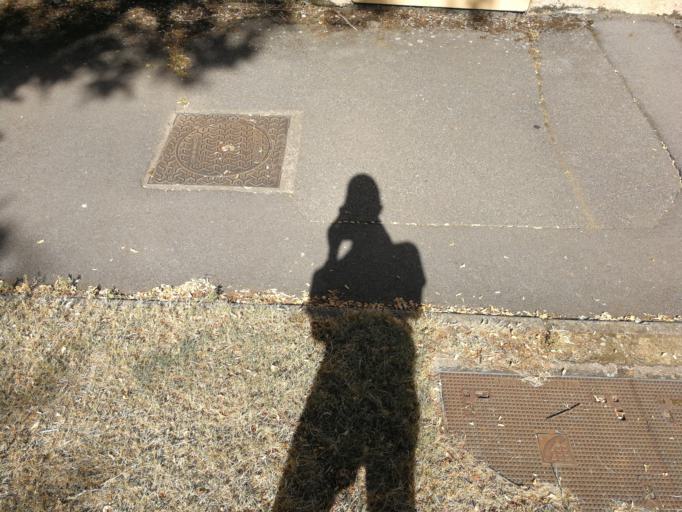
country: FR
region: Midi-Pyrenees
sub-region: Departement de la Haute-Garonne
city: Blagnac
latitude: 43.6354
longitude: 1.3891
